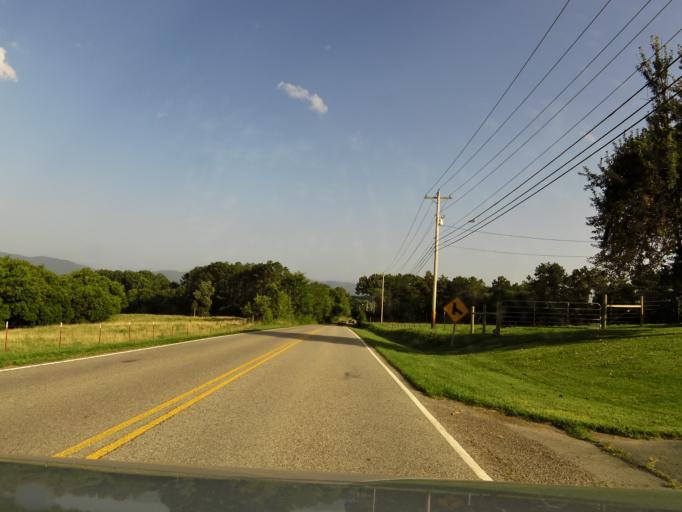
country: US
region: Tennessee
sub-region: Blount County
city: Eagleton Village
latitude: 35.7993
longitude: -83.9069
